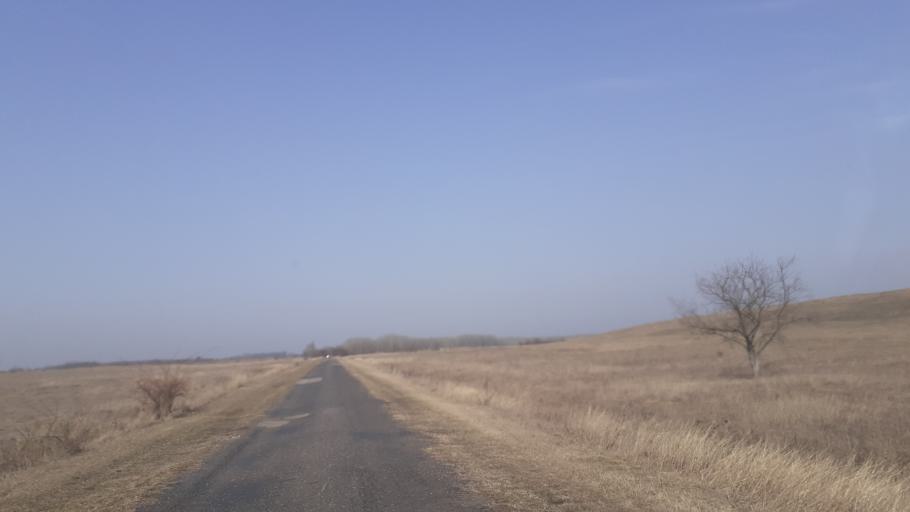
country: HU
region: Pest
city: Dabas
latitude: 47.1025
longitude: 19.2271
